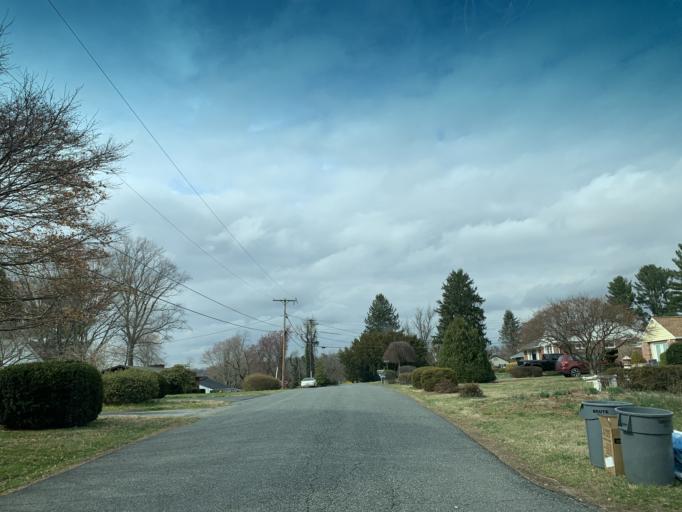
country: US
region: Maryland
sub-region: Harford County
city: North Bel Air
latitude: 39.5186
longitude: -76.3662
